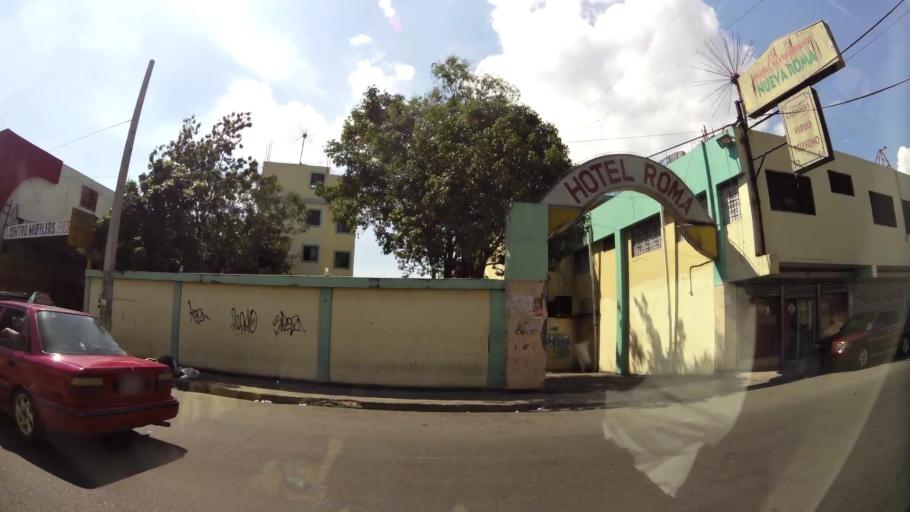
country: DO
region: Nacional
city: Bella Vista
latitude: 18.4713
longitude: -69.9720
